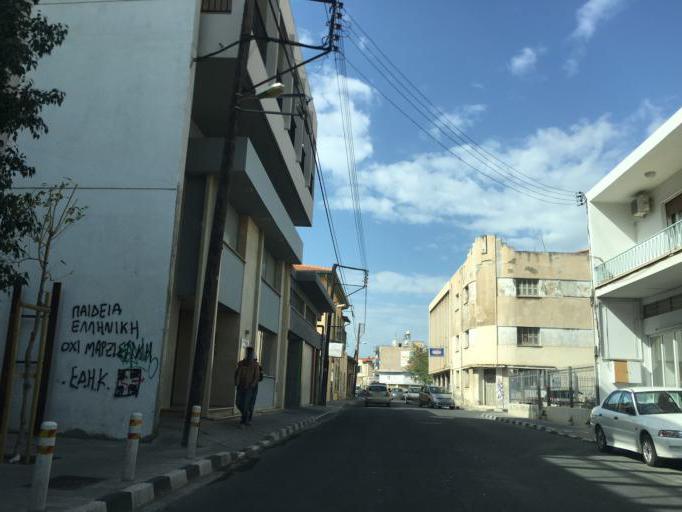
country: CY
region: Limassol
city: Limassol
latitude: 34.6775
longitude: 33.0401
